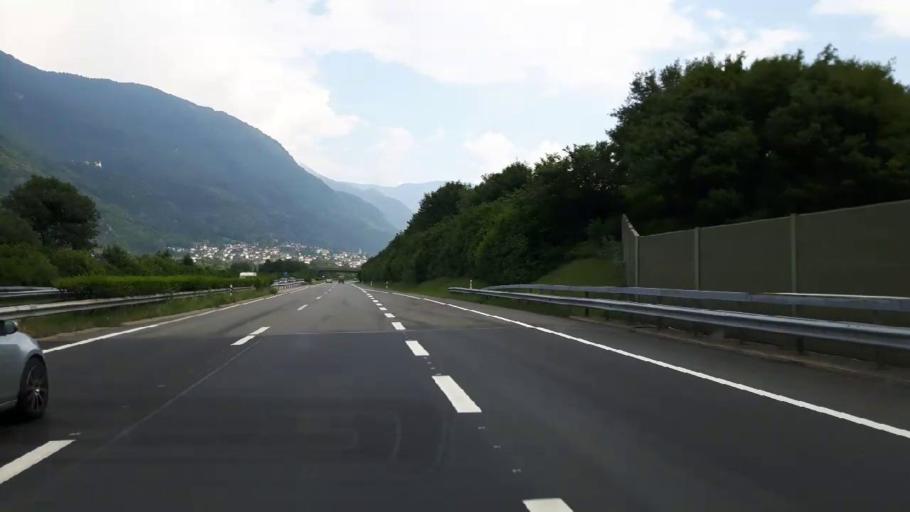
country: CH
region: Ticino
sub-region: Riviera District
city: Claro
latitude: 46.2704
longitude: 9.0018
